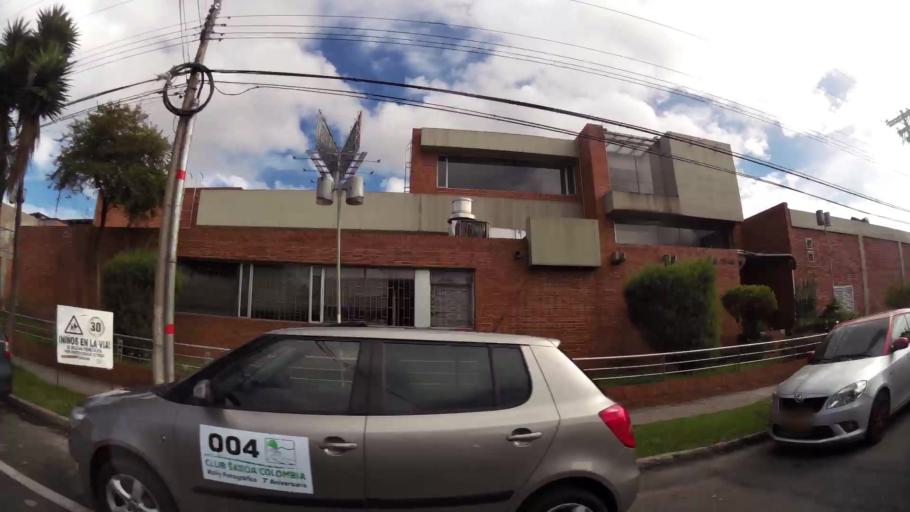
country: CO
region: Bogota D.C.
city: Barrio San Luis
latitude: 4.7102
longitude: -74.0727
